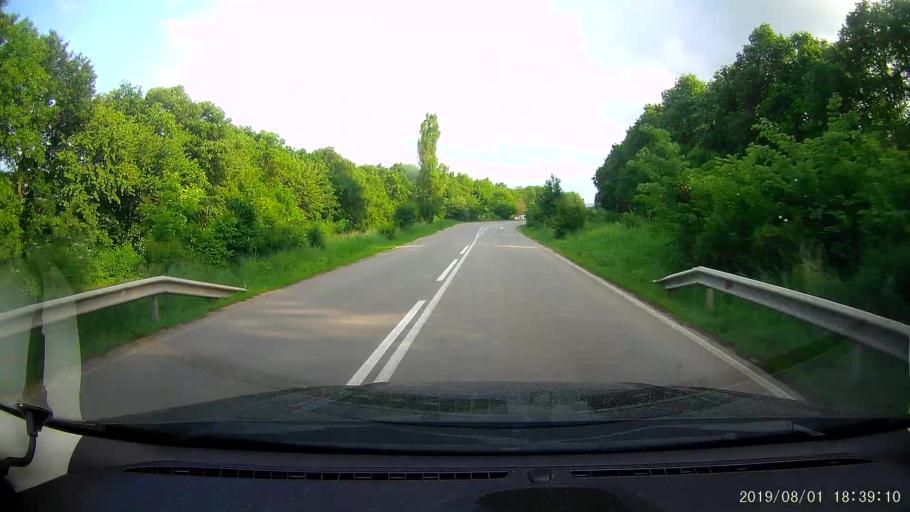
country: BG
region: Shumen
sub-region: Obshtina Khitrino
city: Gara Khitrino
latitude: 43.3910
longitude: 26.9173
